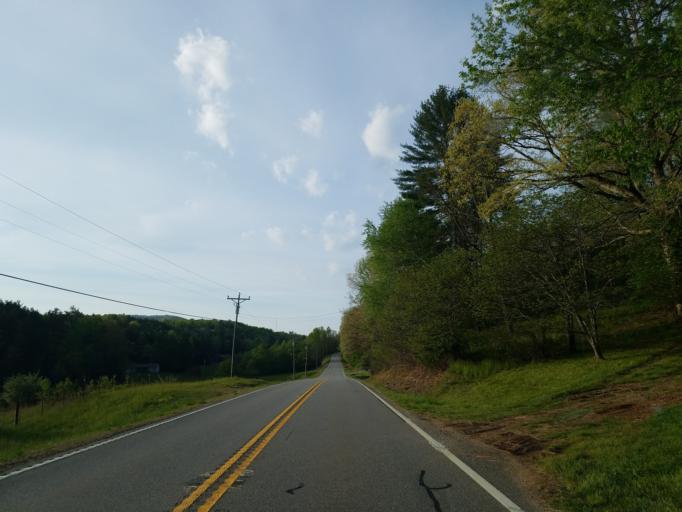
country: US
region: Georgia
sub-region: Fannin County
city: Blue Ridge
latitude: 34.7766
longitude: -84.1854
